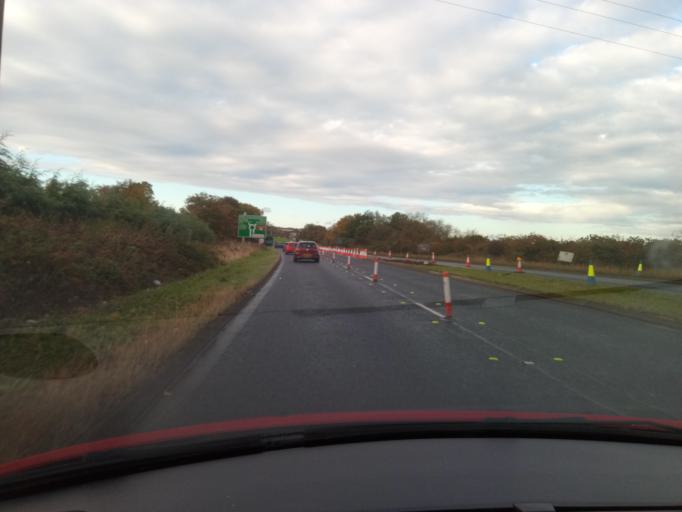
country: GB
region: England
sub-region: Darlington
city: Heighington
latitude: 54.5738
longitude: -1.6109
